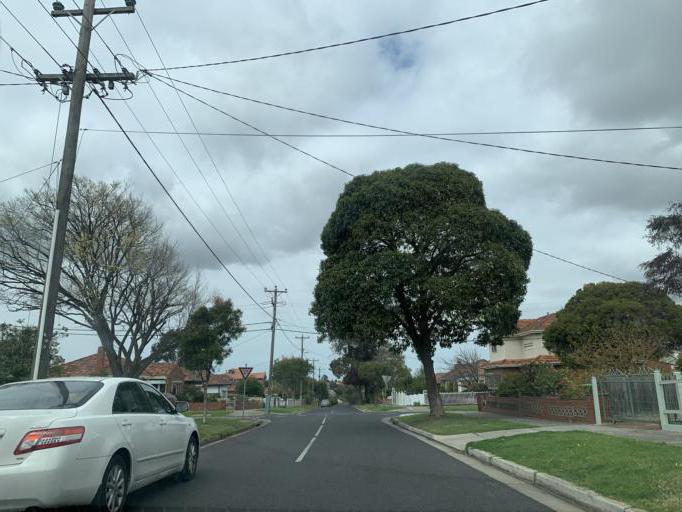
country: AU
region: Victoria
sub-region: Moreland
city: Pascoe Vale South
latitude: -37.7432
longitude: 144.9407
